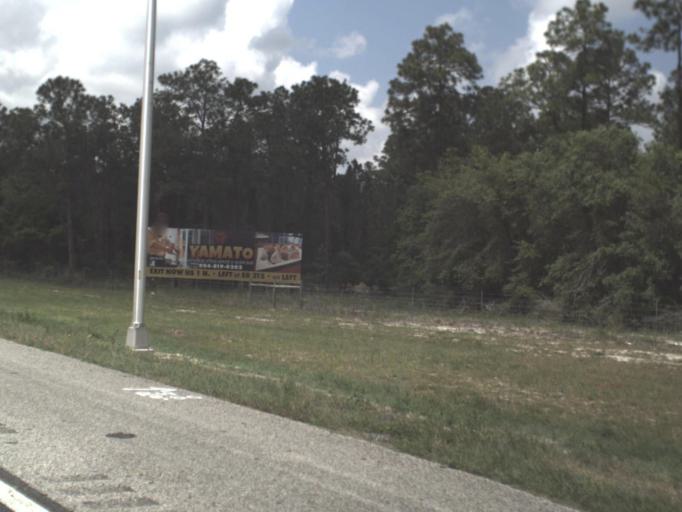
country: US
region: Florida
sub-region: Flagler County
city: Palm Coast
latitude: 29.6593
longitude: -81.2821
